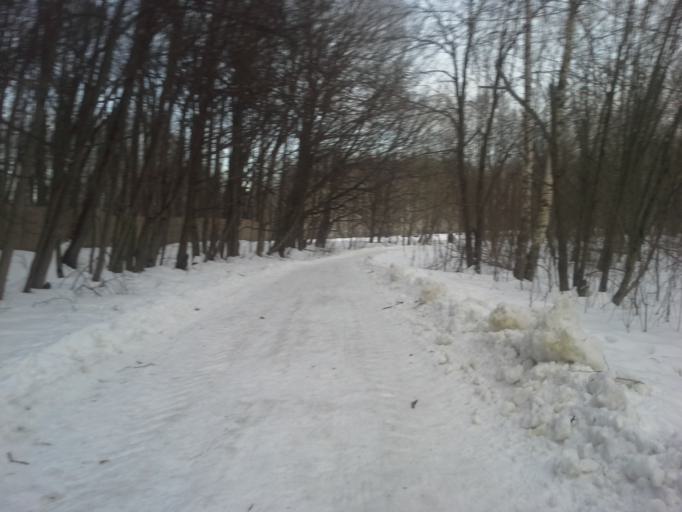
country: RU
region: Moscow
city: Yasenevo
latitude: 55.5954
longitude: 37.5484
